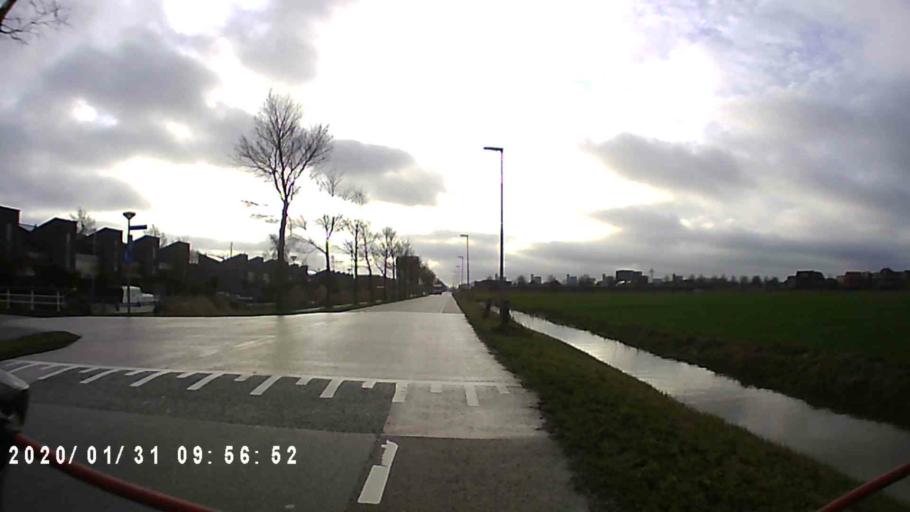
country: NL
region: Groningen
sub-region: Gemeente Groningen
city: Korrewegwijk
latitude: 53.2437
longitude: 6.5202
